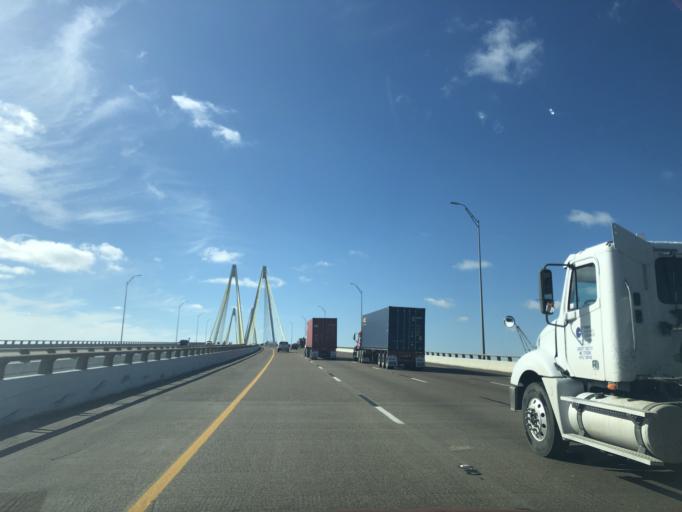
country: US
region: Texas
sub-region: Harris County
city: Baytown
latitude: 29.7082
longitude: -95.0107
